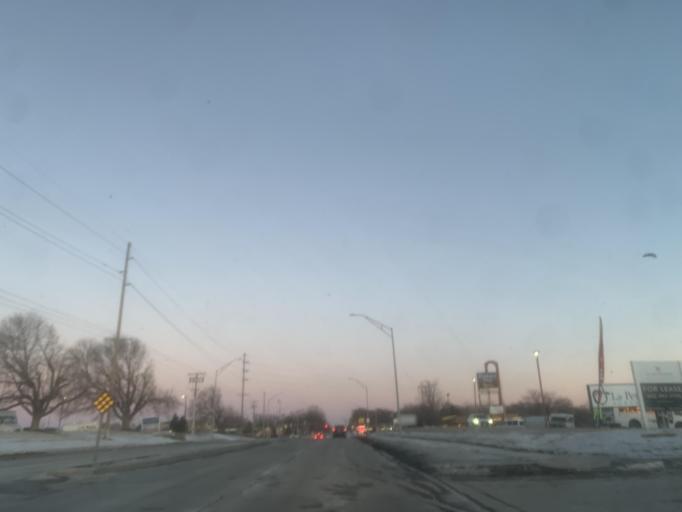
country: US
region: Nebraska
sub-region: Douglas County
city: Ralston
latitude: 41.2053
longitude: -96.0842
